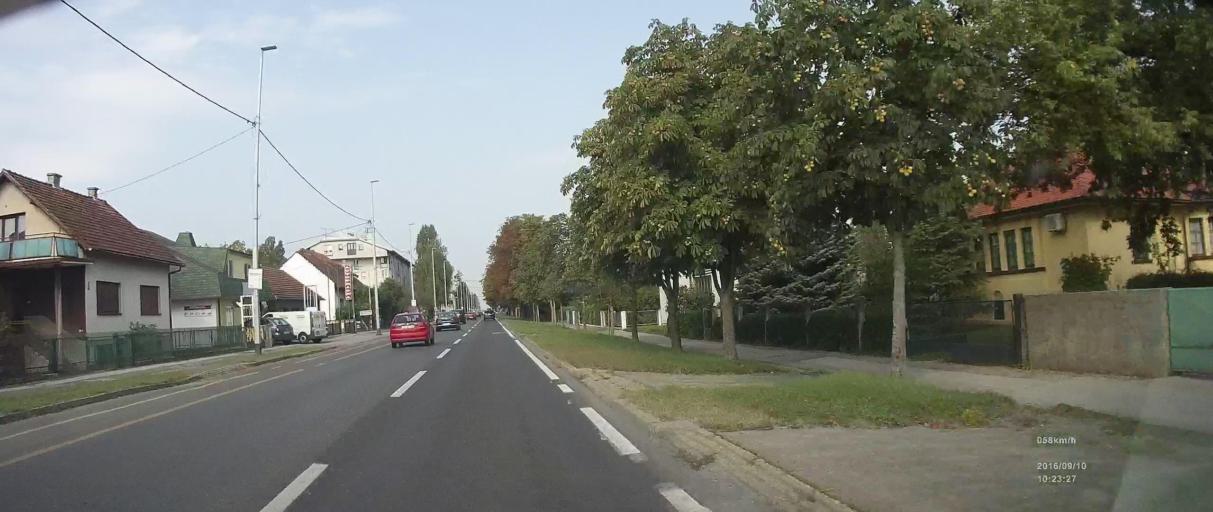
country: HR
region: Zagrebacka
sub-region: Grad Velika Gorica
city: Velika Gorica
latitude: 45.7177
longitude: 16.0652
